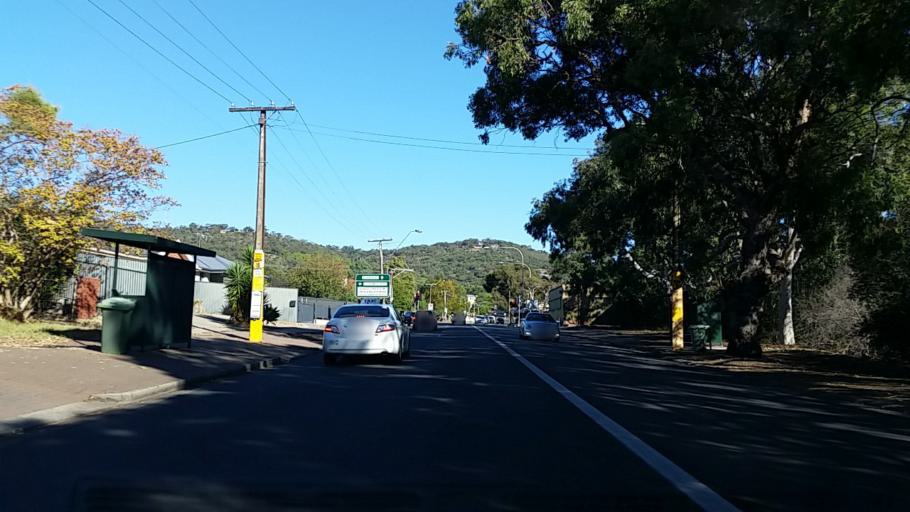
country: AU
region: South Australia
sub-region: Mitcham
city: Hawthorn
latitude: -34.9827
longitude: 138.6113
